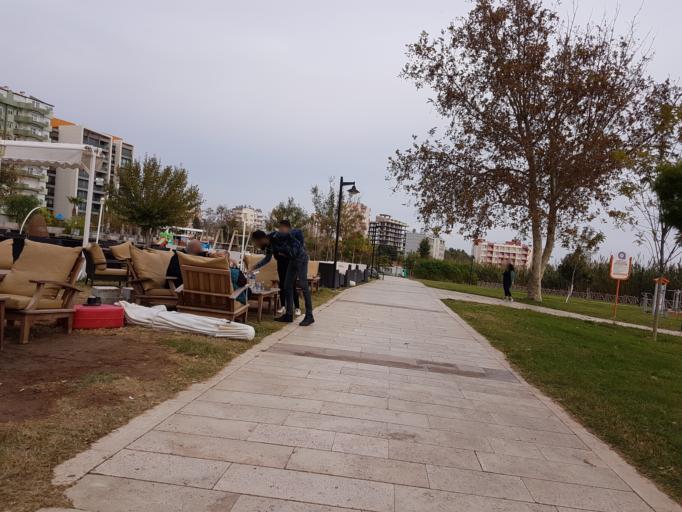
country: TR
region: Antalya
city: Antalya
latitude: 36.8523
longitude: 30.7868
